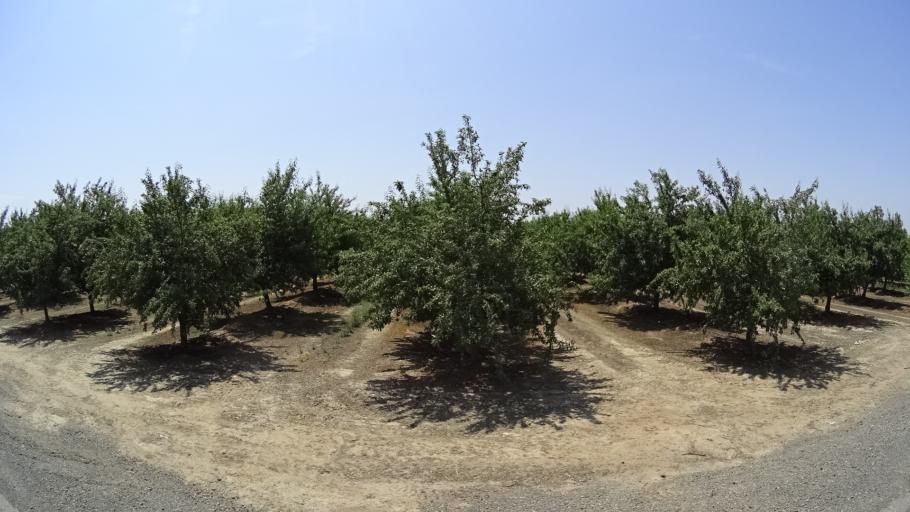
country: US
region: California
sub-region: Kings County
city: Armona
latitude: 36.3280
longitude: -119.7460
